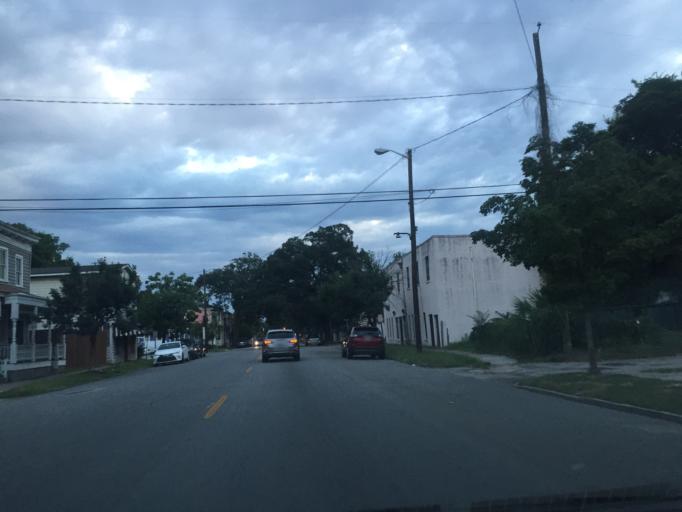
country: US
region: Georgia
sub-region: Chatham County
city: Savannah
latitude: 32.0662
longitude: -81.1015
